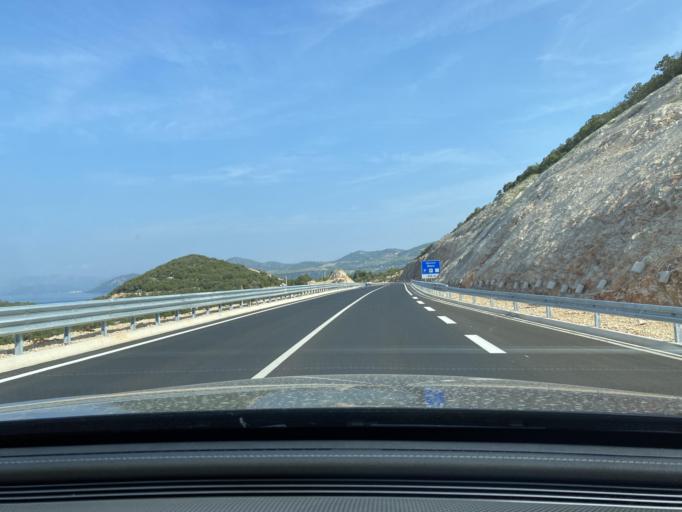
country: BA
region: Federation of Bosnia and Herzegovina
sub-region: Hercegovacko-Bosanski Kanton
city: Neum
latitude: 42.9144
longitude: 17.5280
